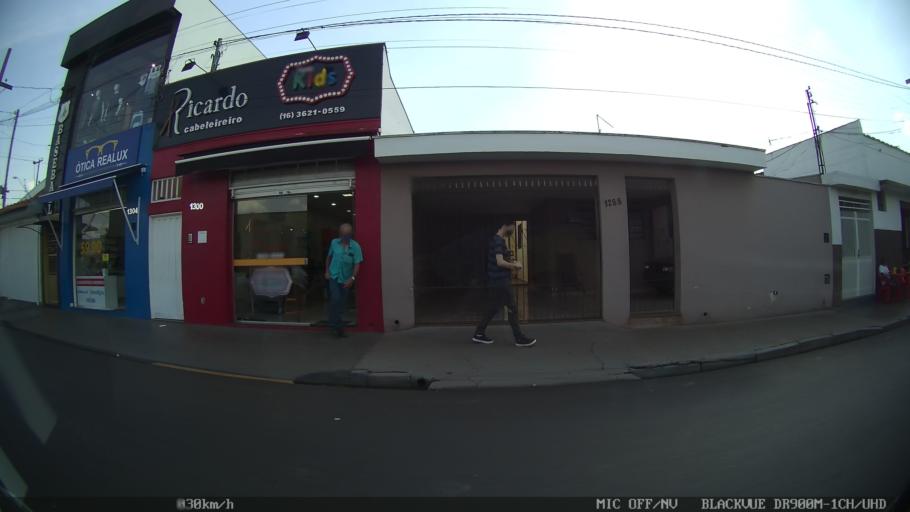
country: BR
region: Sao Paulo
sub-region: Ribeirao Preto
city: Ribeirao Preto
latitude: -21.1887
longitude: -47.8282
